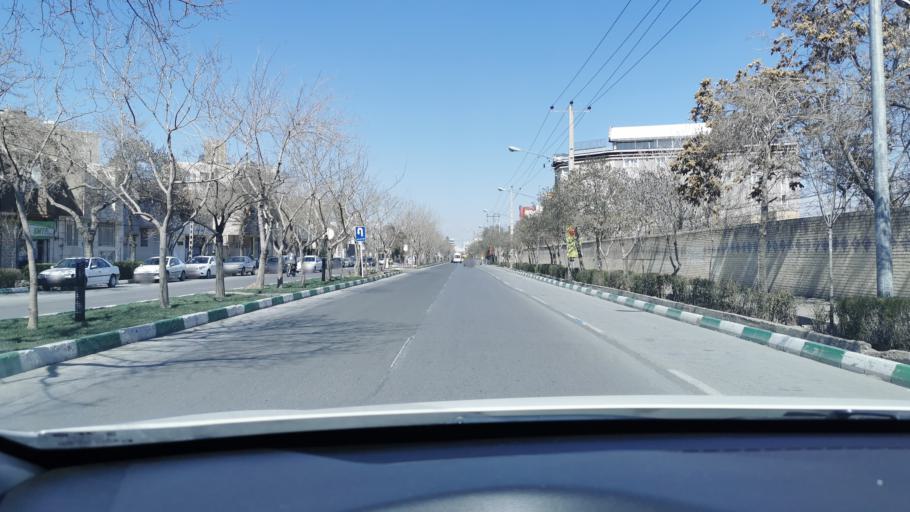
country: IR
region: Razavi Khorasan
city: Mashhad
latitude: 36.2786
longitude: 59.5770
